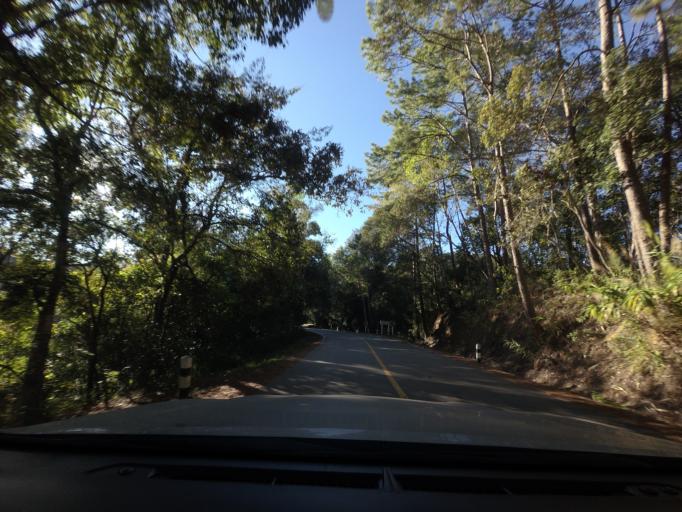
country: TH
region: Mae Hong Son
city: Mae Hi
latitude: 19.2791
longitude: 98.6131
